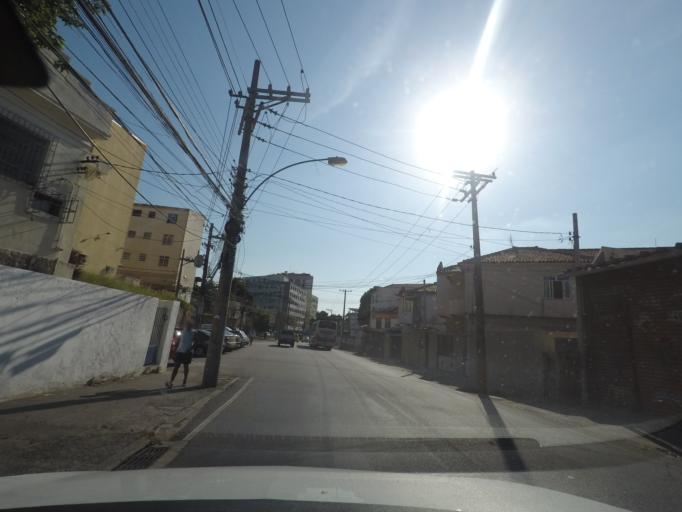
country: BR
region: Rio de Janeiro
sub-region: Duque De Caxias
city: Duque de Caxias
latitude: -22.8423
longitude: -43.2709
